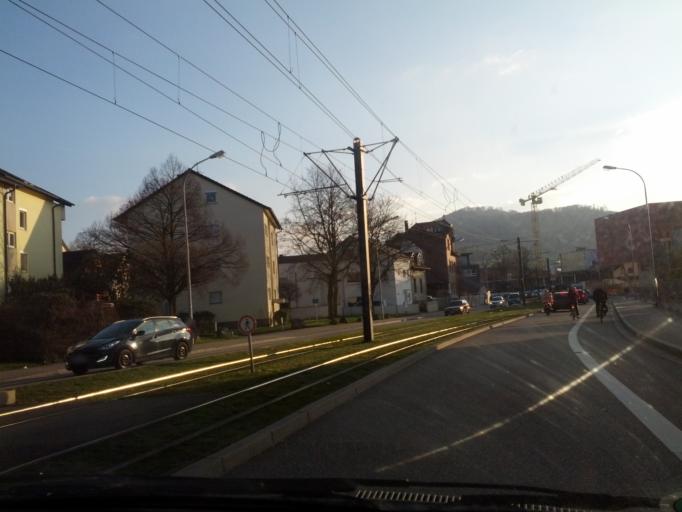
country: DE
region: Baden-Wuerttemberg
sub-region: Freiburg Region
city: Merzhausen
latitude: 47.9784
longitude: 7.8306
